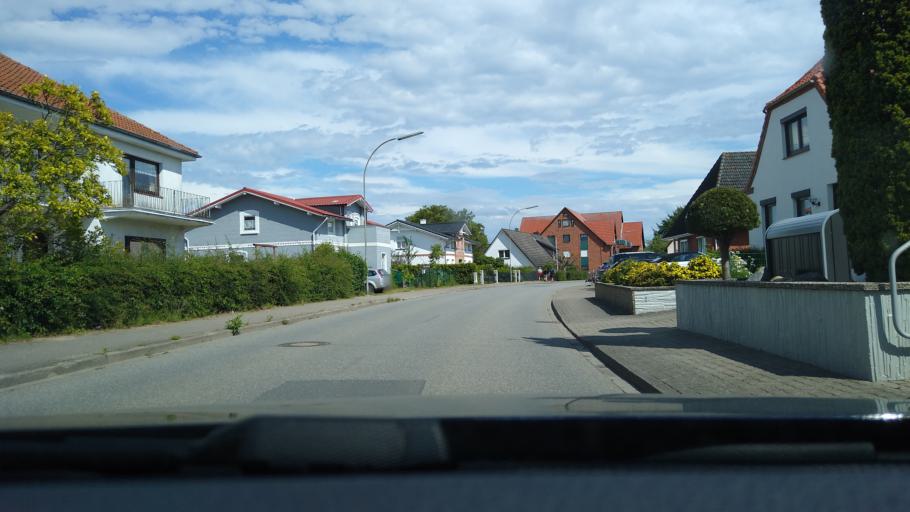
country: DE
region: Schleswig-Holstein
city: Dahme
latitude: 54.2246
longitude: 11.0777
